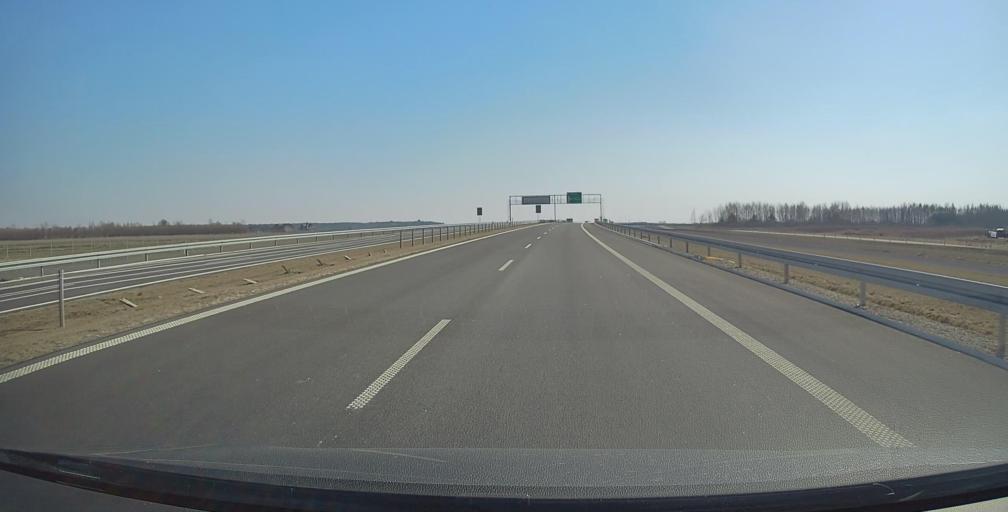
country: PL
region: Lublin Voivodeship
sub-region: Powiat janowski
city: Modliborzyce
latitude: 50.7364
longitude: 22.3396
